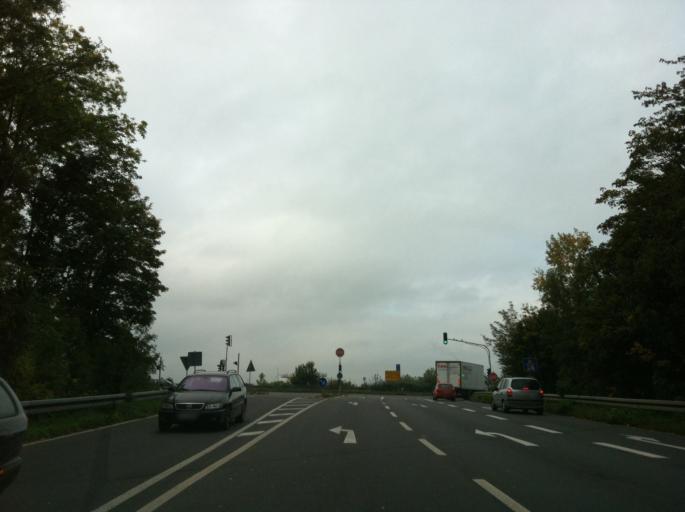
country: DE
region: North Rhine-Westphalia
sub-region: Regierungsbezirk Koln
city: Niederzier
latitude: 50.8402
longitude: 6.4540
